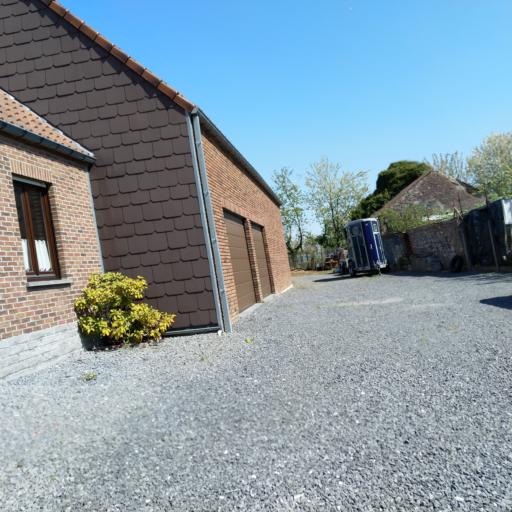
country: BE
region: Wallonia
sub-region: Province du Hainaut
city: Lens
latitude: 50.5583
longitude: 3.8903
